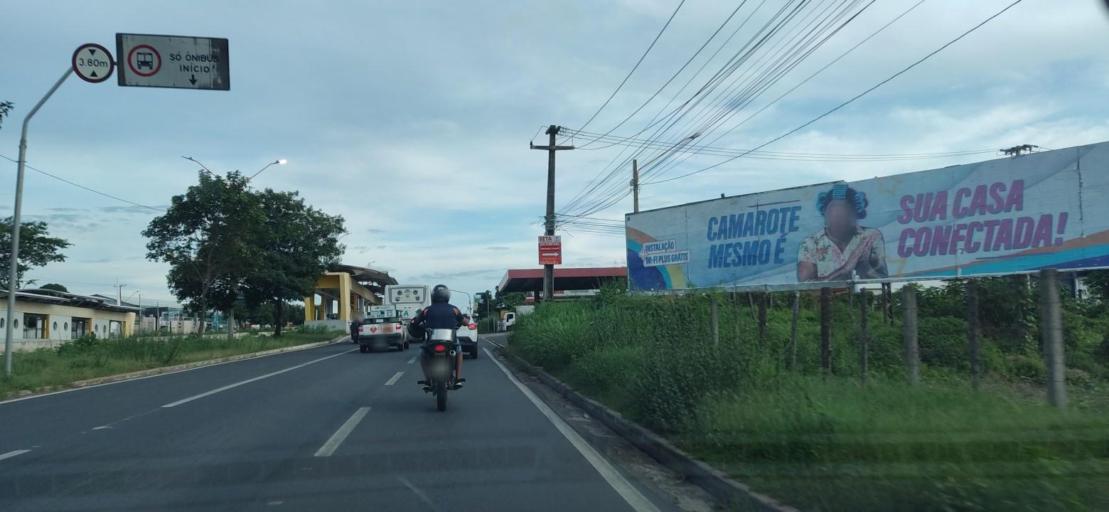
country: BR
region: Piaui
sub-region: Teresina
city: Teresina
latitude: -5.1256
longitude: -42.7945
